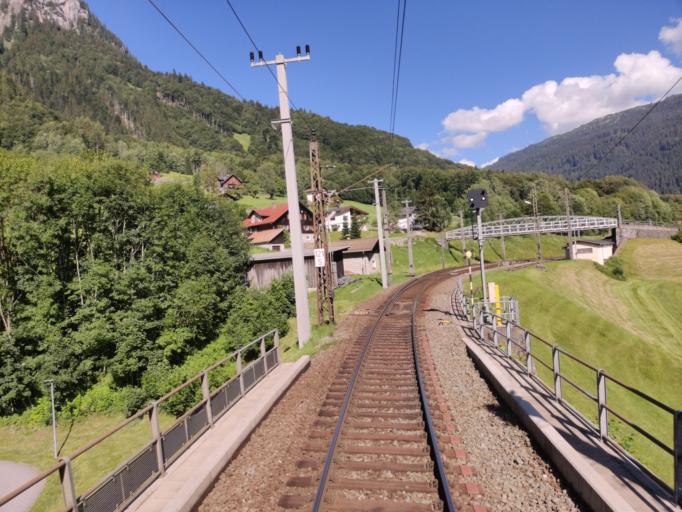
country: AT
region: Vorarlberg
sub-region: Politischer Bezirk Bludenz
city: Dalaas
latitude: 47.1289
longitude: 9.9890
